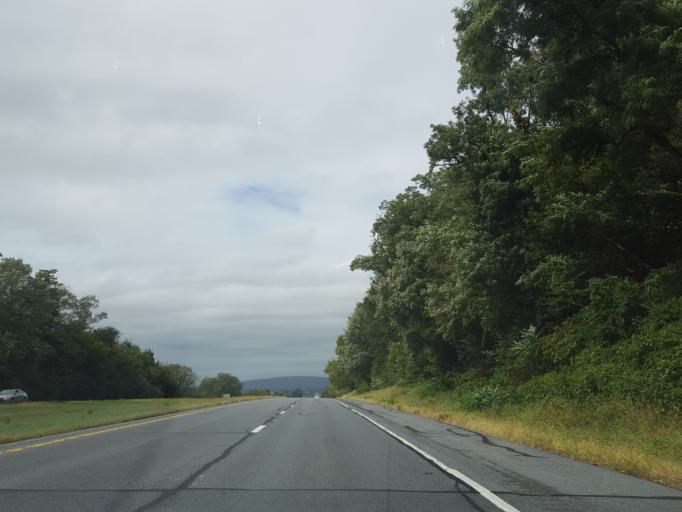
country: US
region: Maryland
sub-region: Frederick County
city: Jefferson
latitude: 39.3589
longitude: -77.5378
